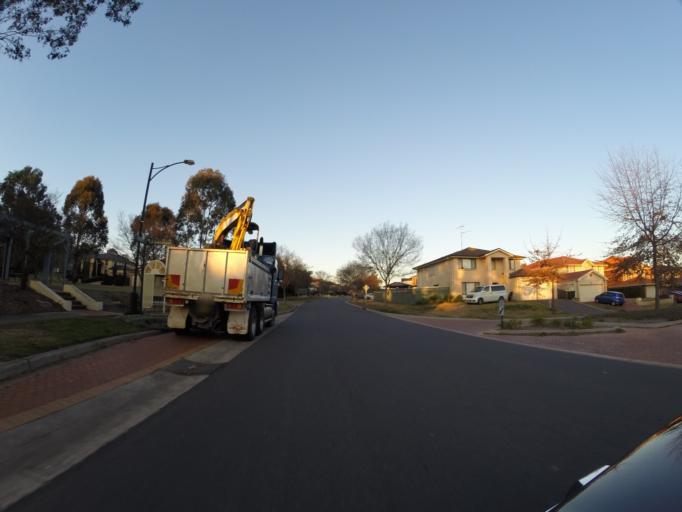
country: AU
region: New South Wales
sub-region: Camden
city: Narellan
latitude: -34.0233
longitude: 150.7335
